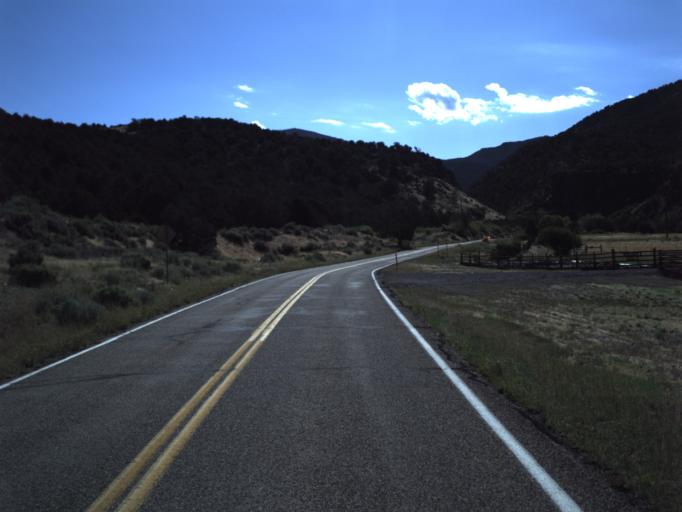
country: US
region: Utah
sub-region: Beaver County
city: Beaver
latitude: 38.2829
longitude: -112.5832
